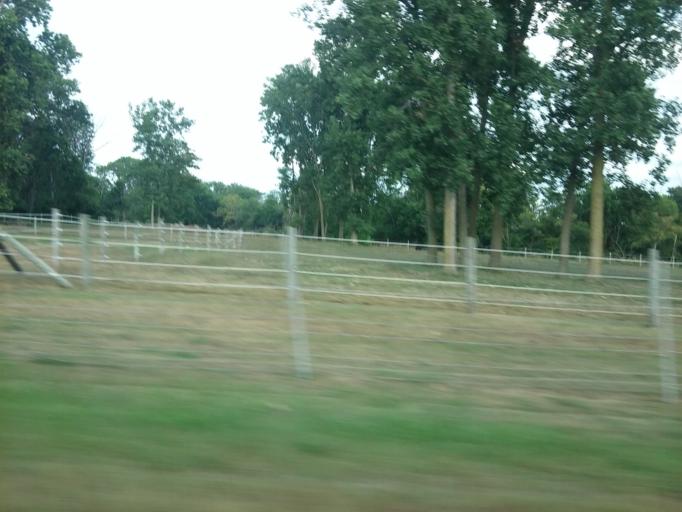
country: US
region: Ohio
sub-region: Wood County
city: Bowling Green
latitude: 41.3000
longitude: -83.6503
